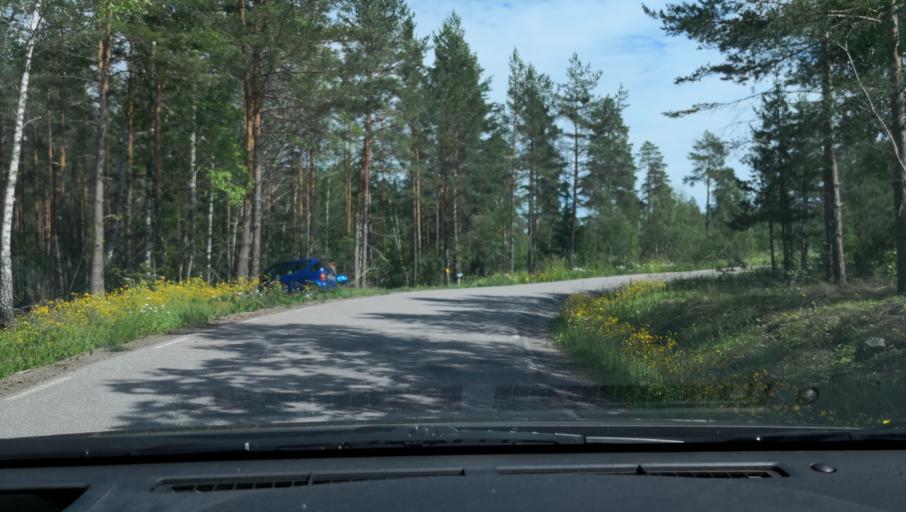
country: SE
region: Uppsala
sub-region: Uppsala Kommun
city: Alsike
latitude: 59.7056
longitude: 17.6769
